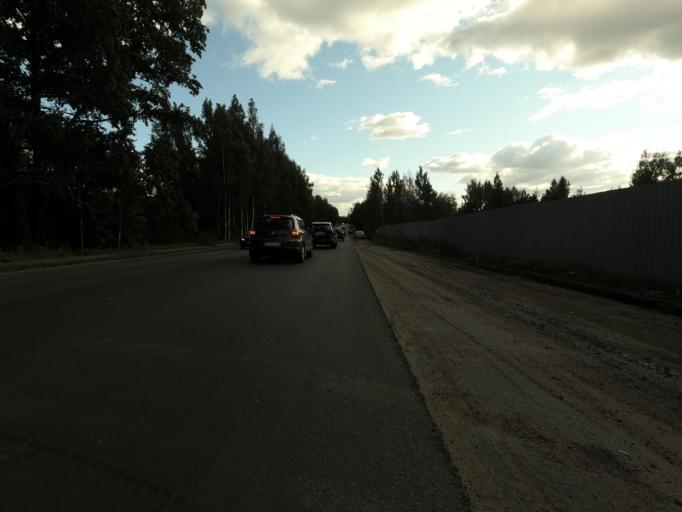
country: RU
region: Leningrad
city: Vsevolozhsk
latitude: 59.9761
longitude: 30.6535
